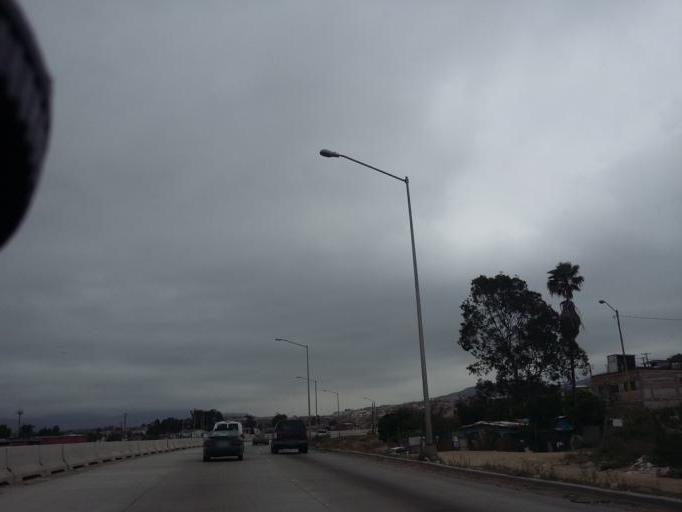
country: MX
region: Baja California
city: Tijuana
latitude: 32.5139
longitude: -116.9540
